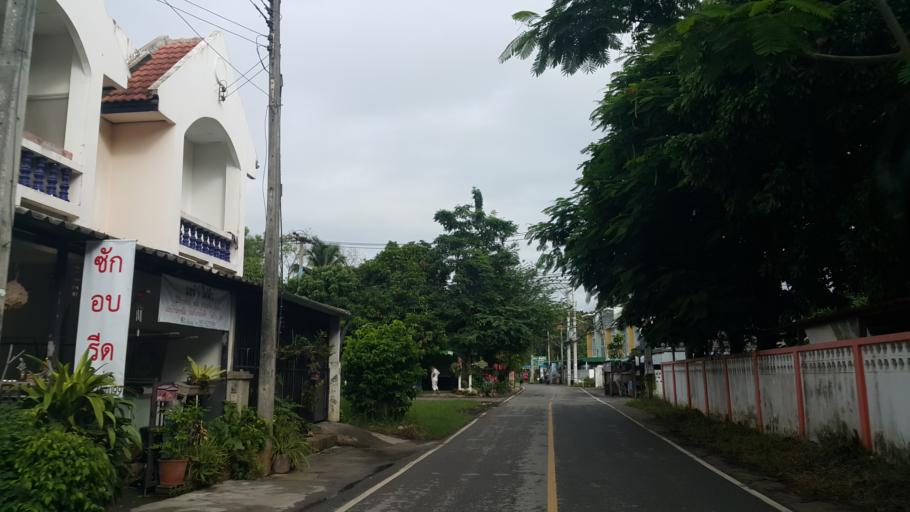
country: TH
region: Chiang Mai
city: Chiang Mai
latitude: 18.7476
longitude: 98.9701
